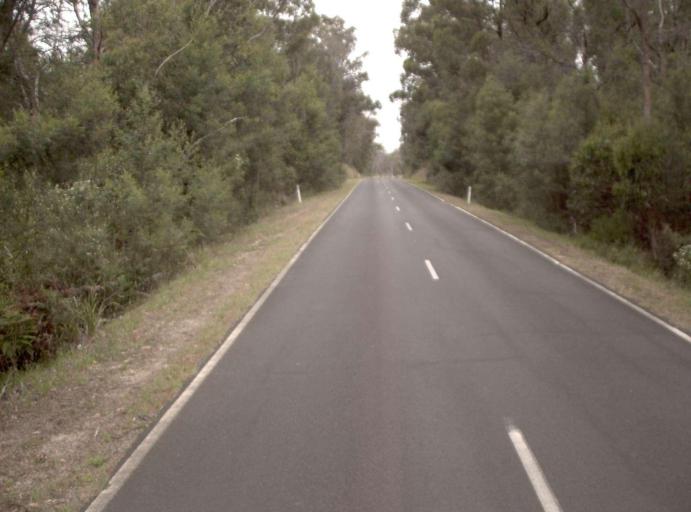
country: AU
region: Victoria
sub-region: Latrobe
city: Traralgon
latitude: -38.4516
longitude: 146.8224
